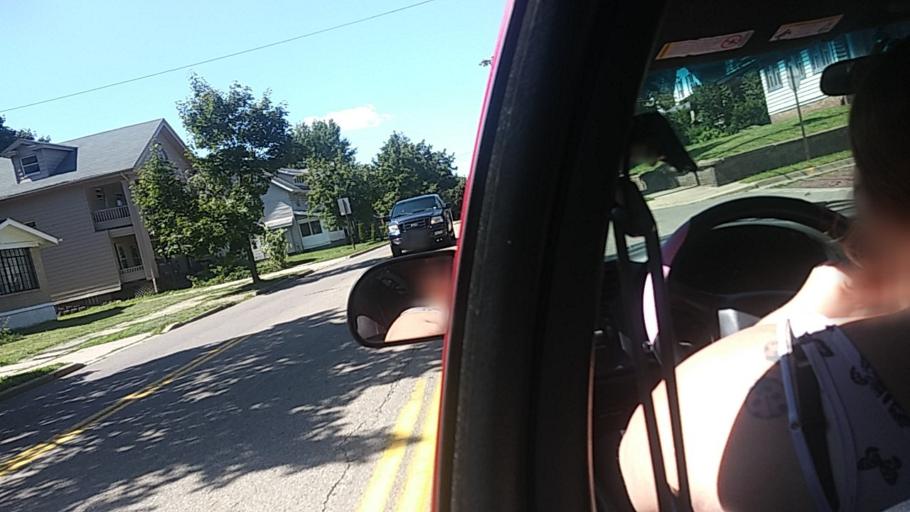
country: US
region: Ohio
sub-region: Summit County
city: Akron
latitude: 41.0953
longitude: -81.5503
